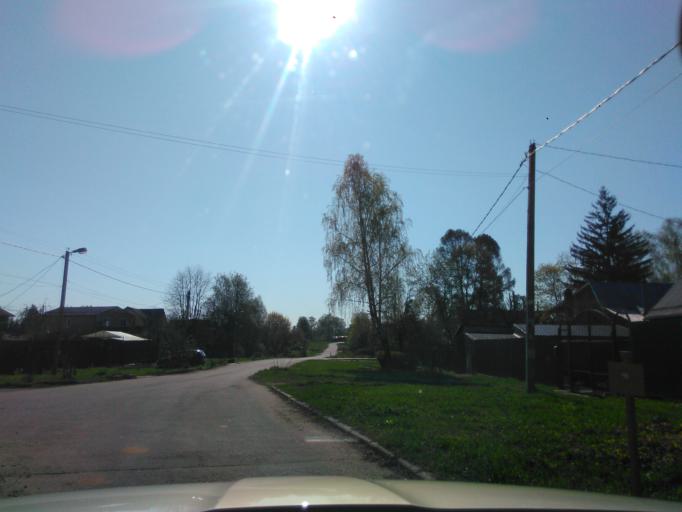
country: RU
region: Moskovskaya
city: Firsanovka
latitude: 55.9609
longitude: 37.2695
